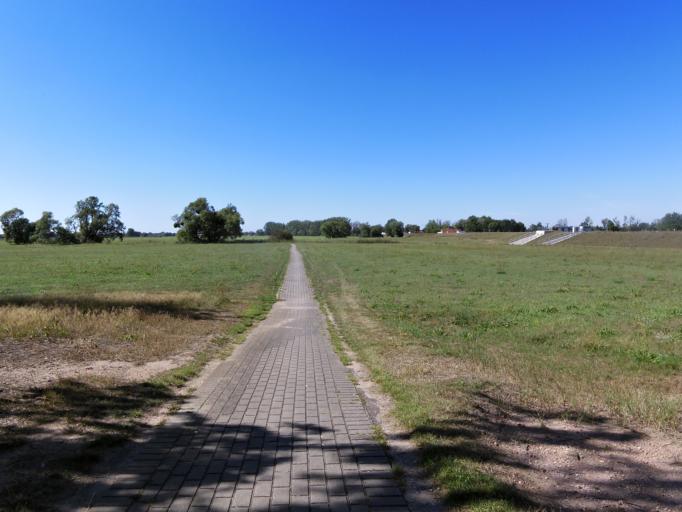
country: DE
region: Saxony-Anhalt
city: Elster
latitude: 51.8315
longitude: 12.8010
